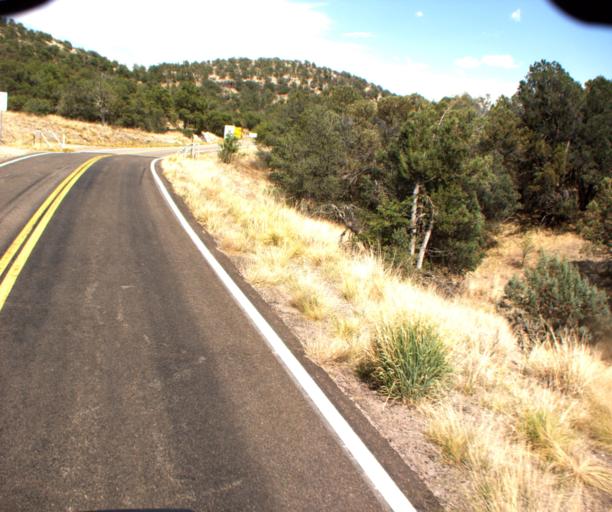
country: US
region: Arizona
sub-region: Greenlee County
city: Clifton
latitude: 33.1073
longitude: -109.0482
